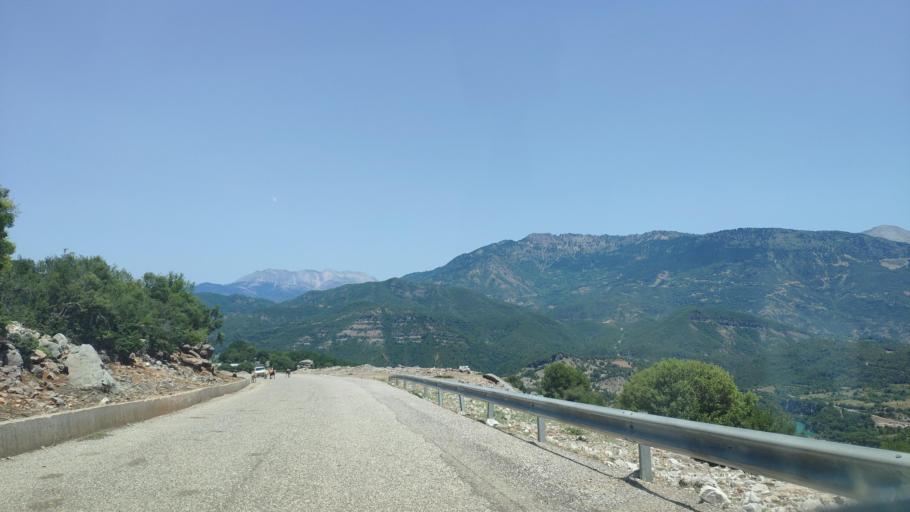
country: GR
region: Thessaly
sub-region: Nomos Kardhitsas
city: Anthiro
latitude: 39.1484
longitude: 21.3870
